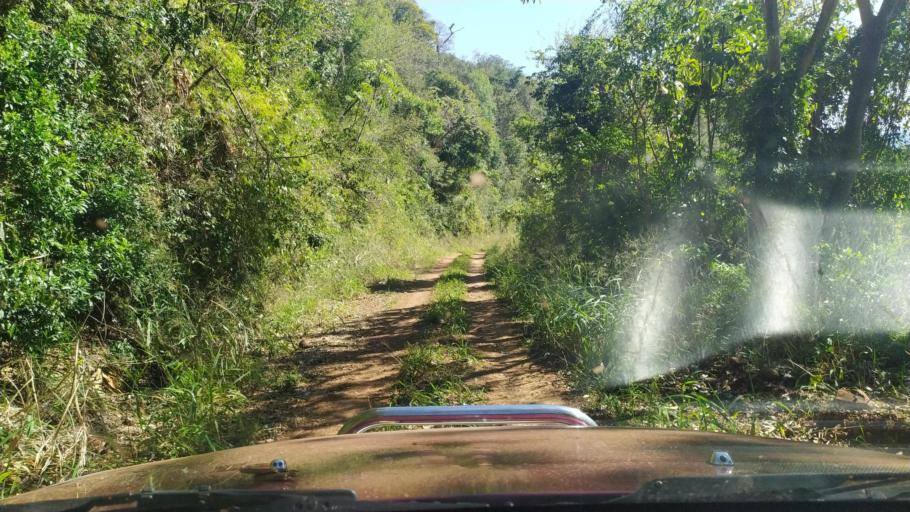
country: AR
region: Misiones
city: El Alcazar
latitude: -26.7653
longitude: -54.5757
